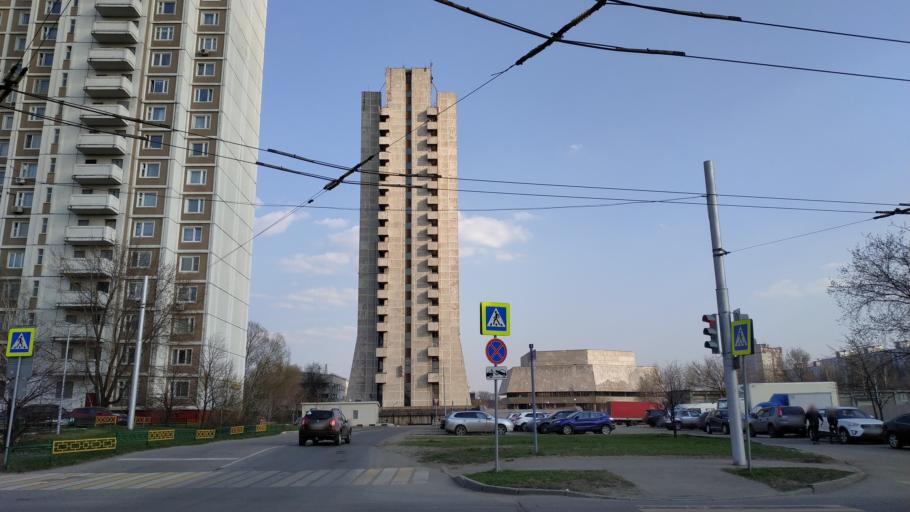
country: RU
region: Moscow
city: Vykhino-Zhulebino
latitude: 55.7037
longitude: 37.8247
